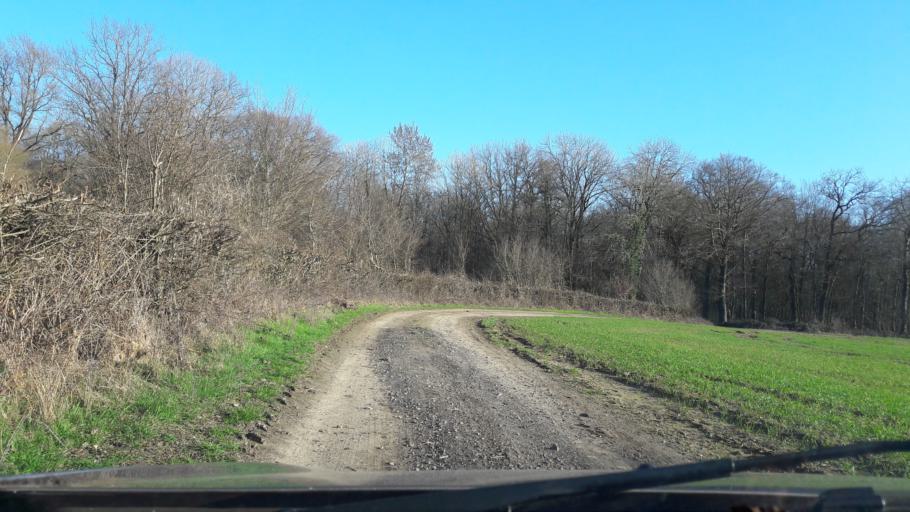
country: BE
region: Wallonia
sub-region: Province du Hainaut
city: Beaumont
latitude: 50.2462
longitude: 4.1991
